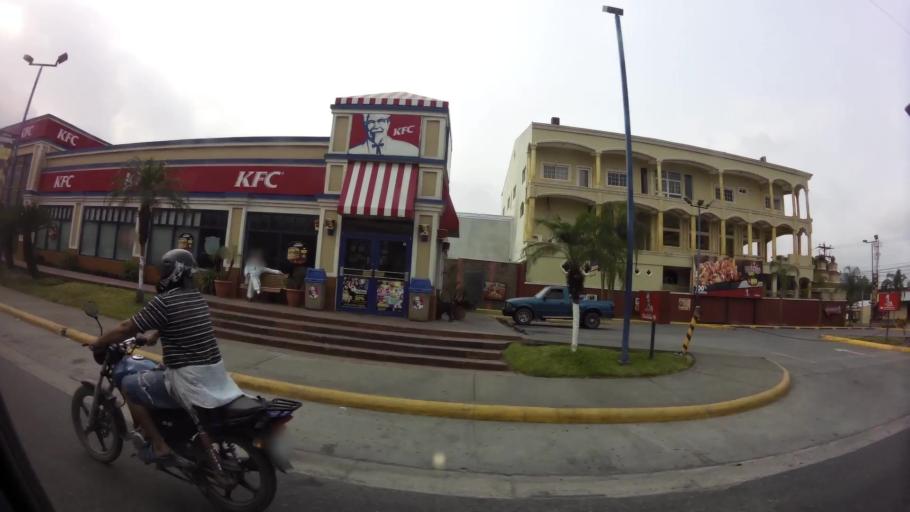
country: HN
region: Yoro
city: El Progreso
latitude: 15.4041
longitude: -87.8106
